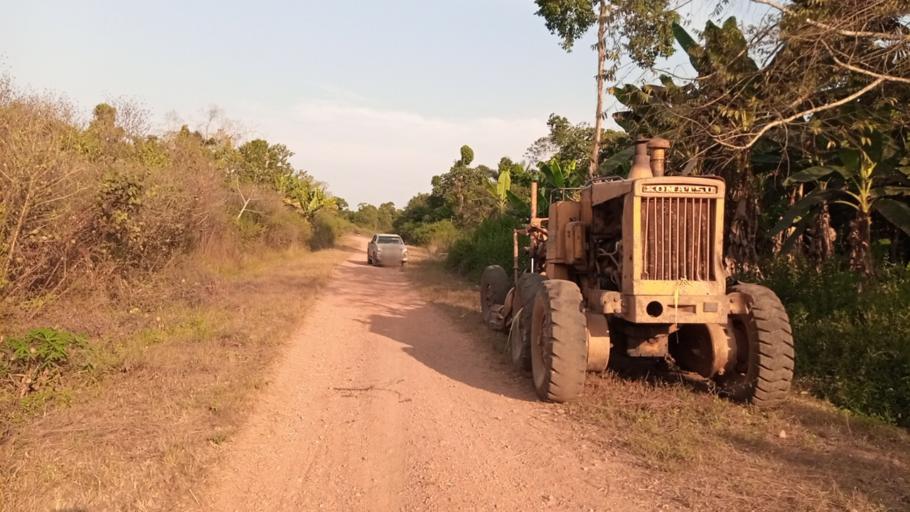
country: NG
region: Osun
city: Ifetedo
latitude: 7.0121
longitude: 4.4125
